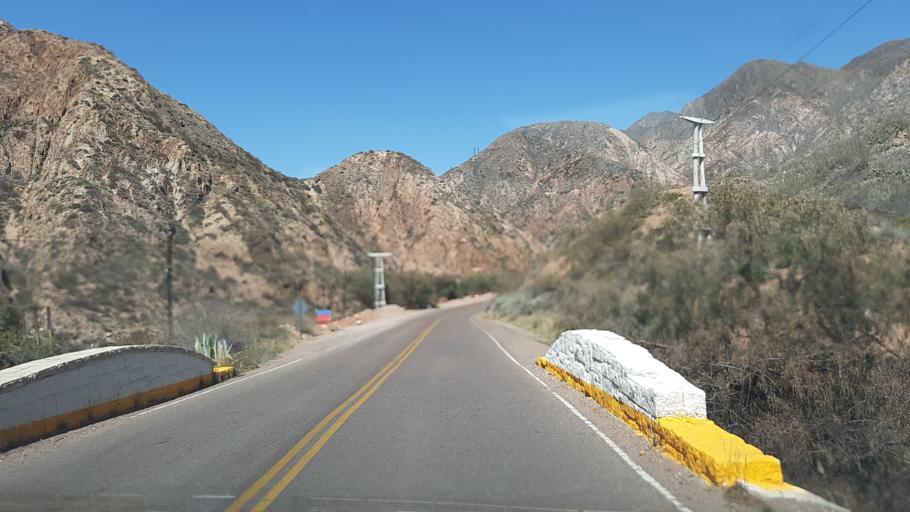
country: AR
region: Mendoza
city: Lujan de Cuyo
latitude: -33.0217
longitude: -69.1146
